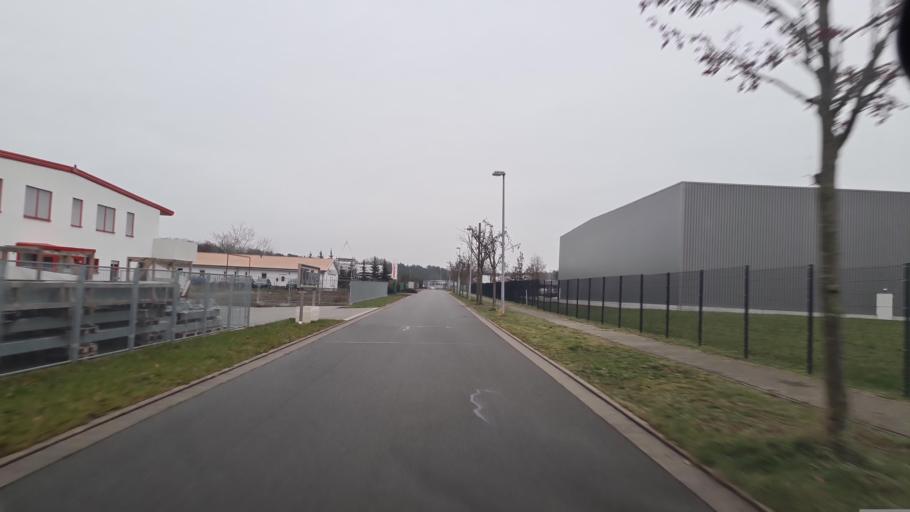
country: DE
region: Brandenburg
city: Werben
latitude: 51.7612
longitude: 14.1588
